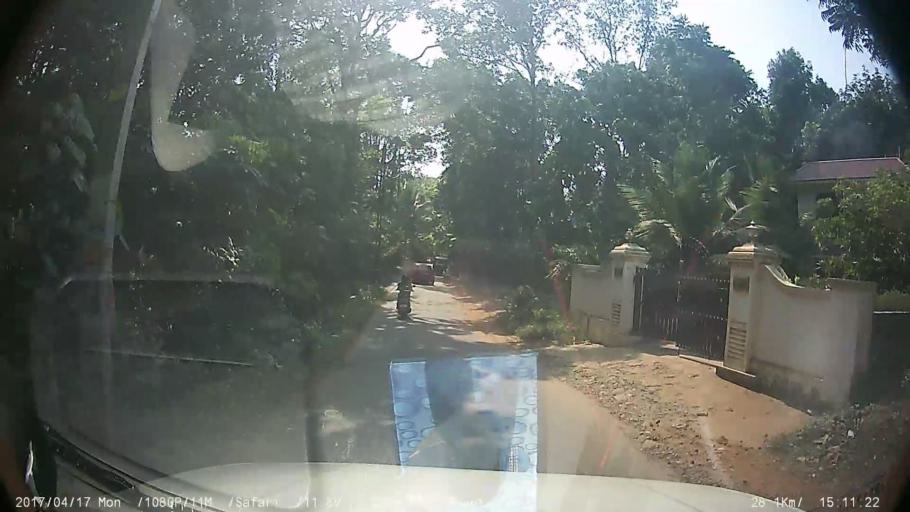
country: IN
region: Kerala
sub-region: Ernakulam
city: Piravam
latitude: 9.8942
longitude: 76.4842
